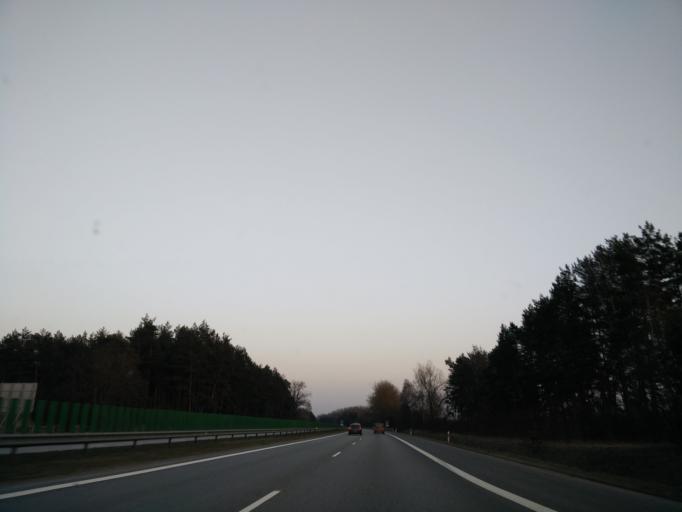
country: LT
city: Lentvaris
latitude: 54.7001
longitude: 25.0110
